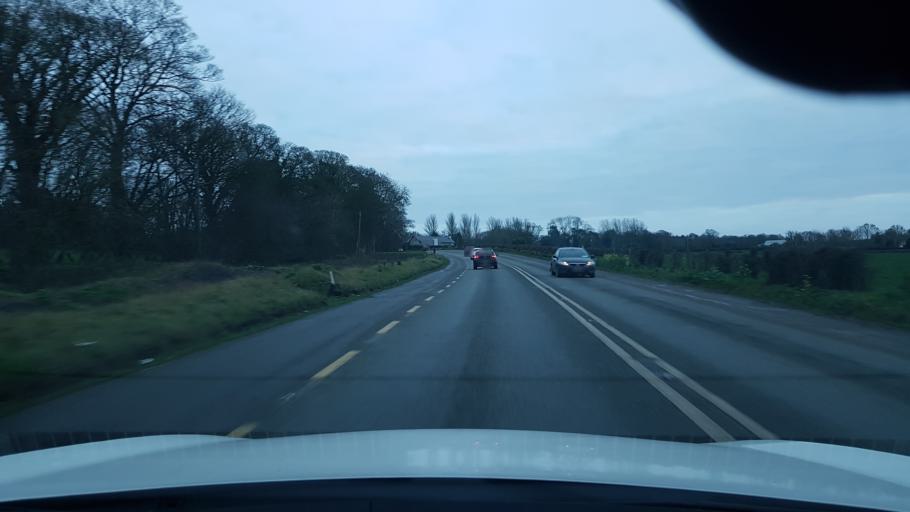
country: IE
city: Kentstown
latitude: 53.5957
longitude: -6.6078
